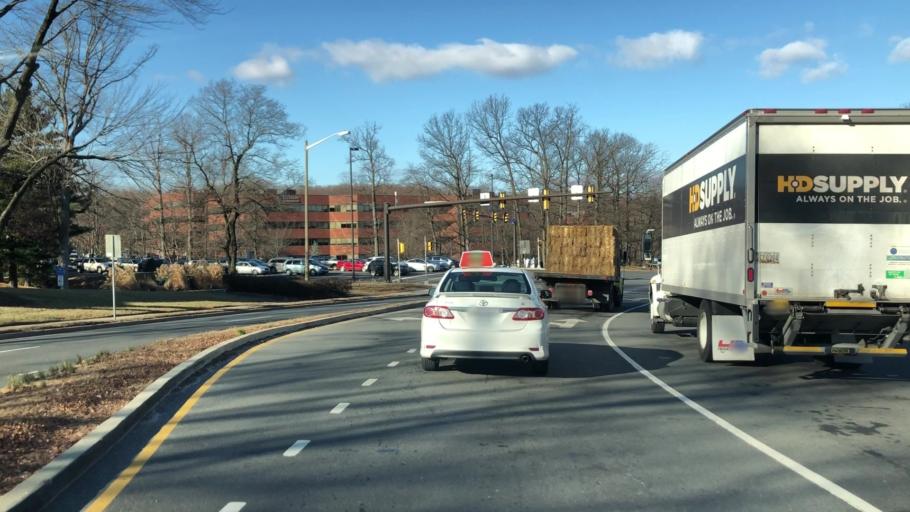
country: US
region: Virginia
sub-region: Fairfax County
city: Reston
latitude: 38.9457
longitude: -77.3579
